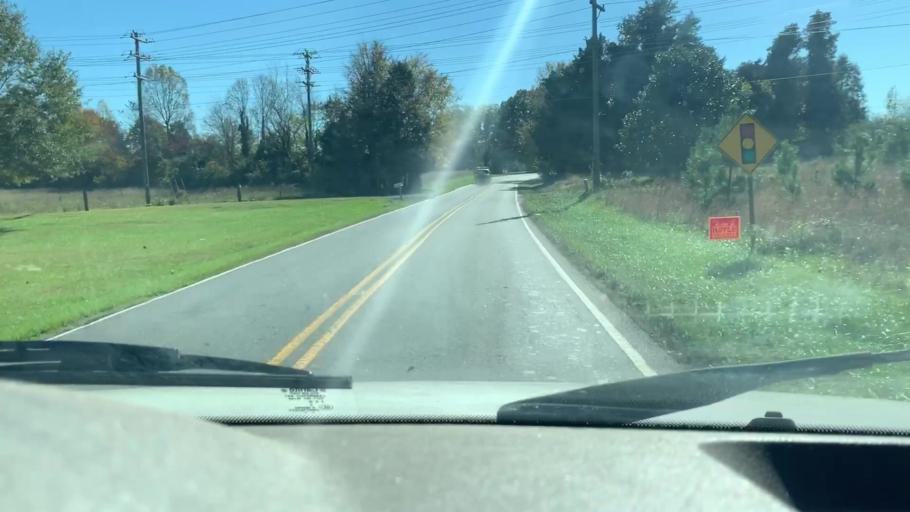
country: US
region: North Carolina
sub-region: Lincoln County
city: Lowesville
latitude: 35.4459
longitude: -80.9897
